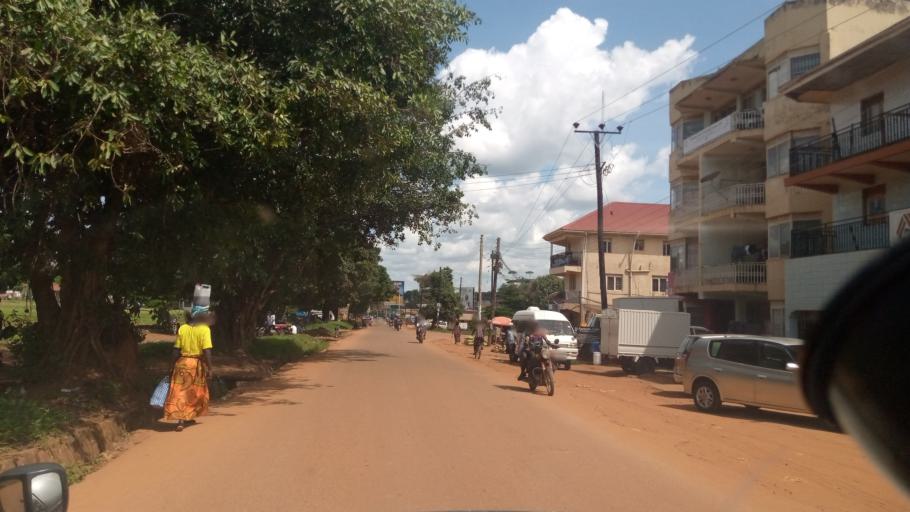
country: UG
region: Northern Region
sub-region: Lira District
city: Lira
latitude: 2.2481
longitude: 32.8985
